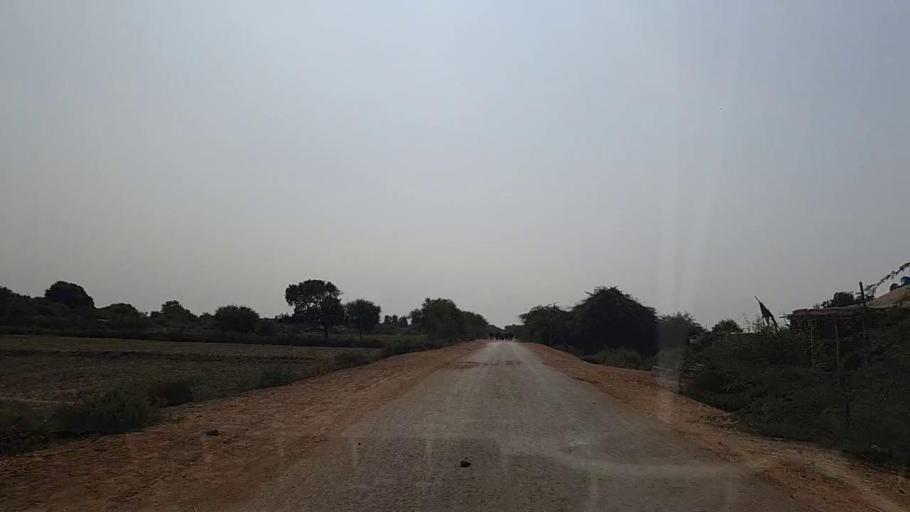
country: PK
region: Sindh
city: Chuhar Jamali
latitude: 24.2551
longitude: 67.9067
